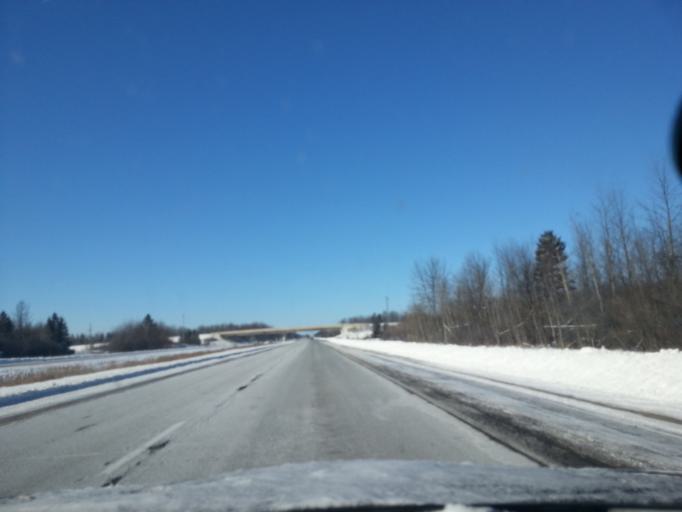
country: CA
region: Ontario
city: Carleton Place
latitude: 45.3123
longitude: -76.0522
